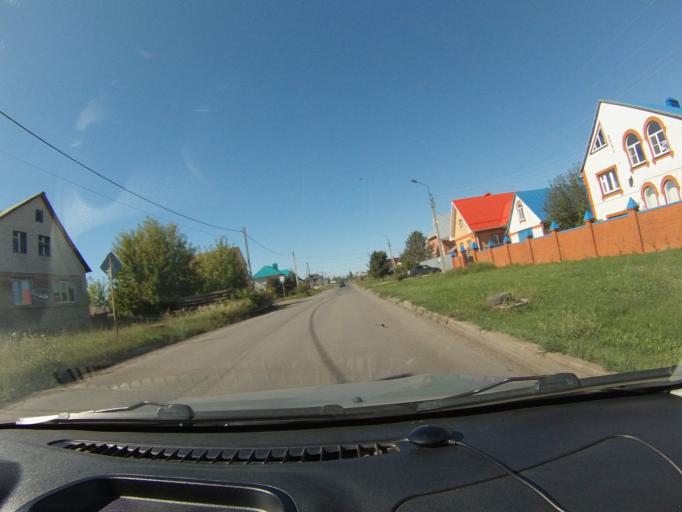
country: RU
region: Tambov
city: Tambov
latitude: 52.7625
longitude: 41.3721
